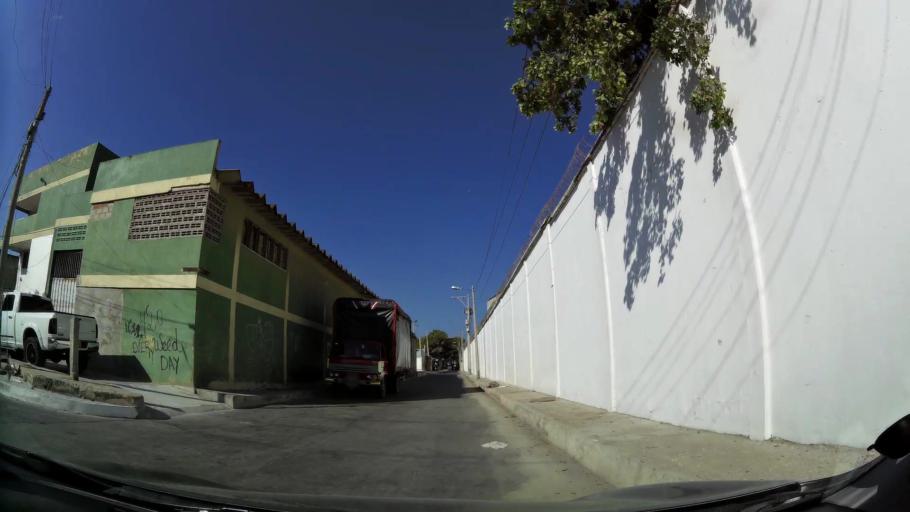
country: CO
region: Atlantico
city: Barranquilla
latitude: 10.9939
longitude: -74.7819
